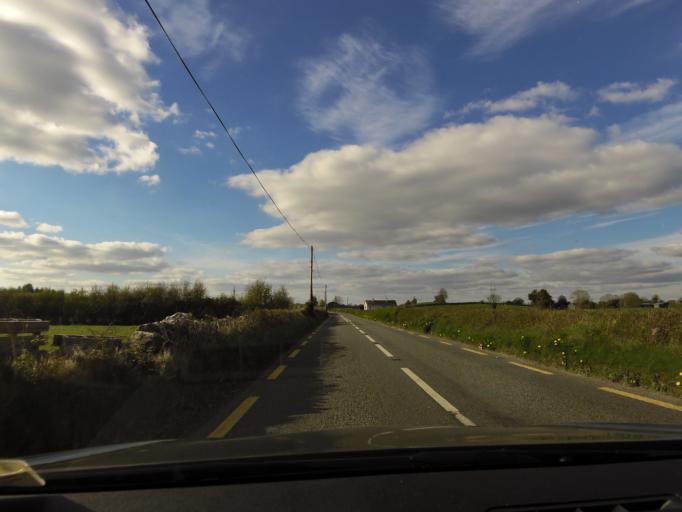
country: IE
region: Connaught
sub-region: County Galway
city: Portumna
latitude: 53.1354
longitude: -8.2490
